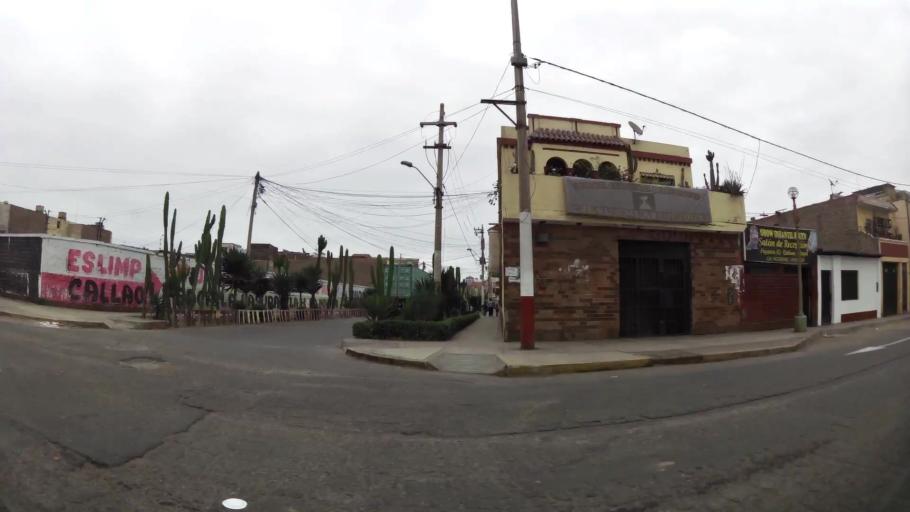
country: PE
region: Callao
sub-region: Callao
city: Callao
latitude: -12.0537
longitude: -77.1337
